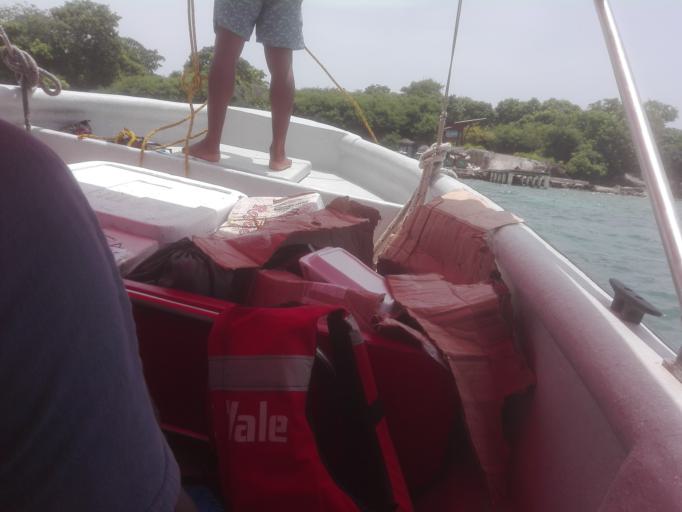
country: CO
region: Bolivar
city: Turbana
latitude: 10.1766
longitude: -75.7299
